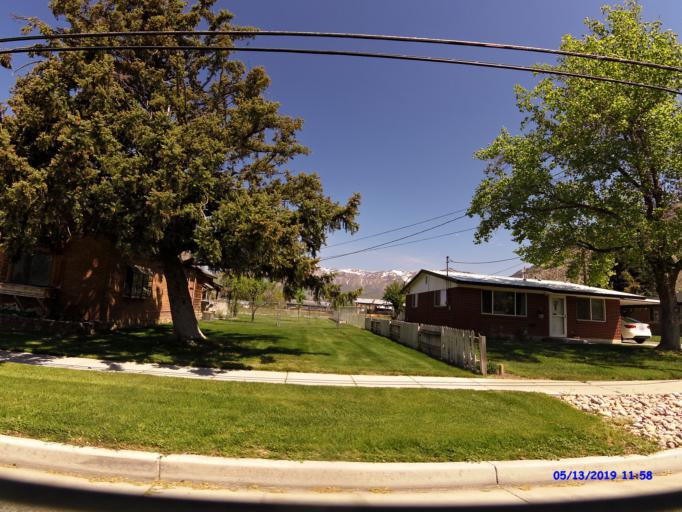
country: US
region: Utah
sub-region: Weber County
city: Harrisville
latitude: 41.2665
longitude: -111.9571
